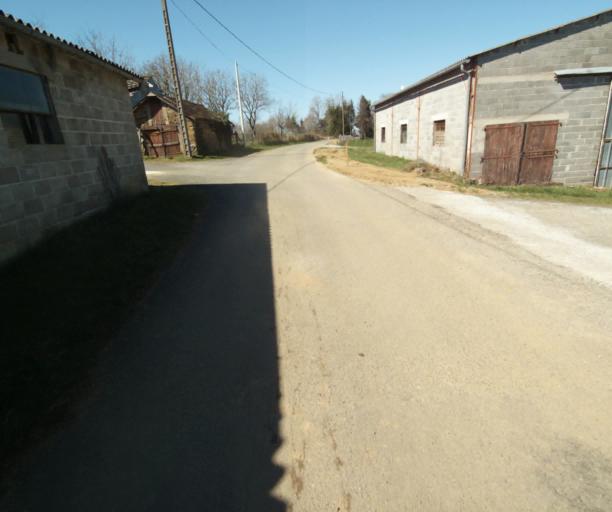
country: FR
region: Limousin
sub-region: Departement de la Correze
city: Saint-Clement
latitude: 45.3736
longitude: 1.6811
